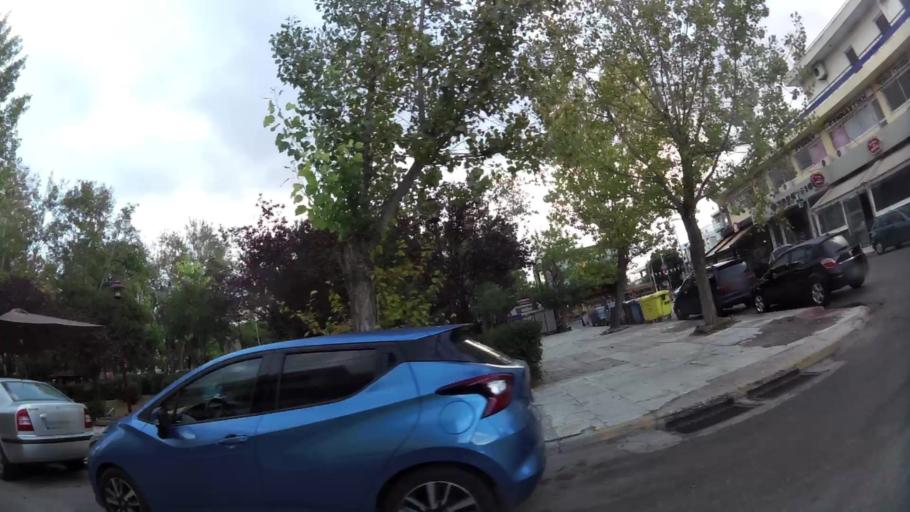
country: GR
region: Attica
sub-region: Nomarchia Athinas
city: Vrilissia
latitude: 38.0375
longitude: 23.8264
